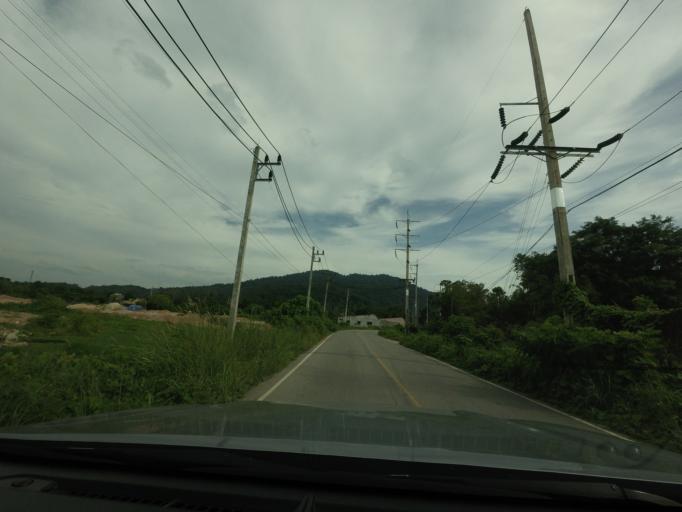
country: TH
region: Yala
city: Yala
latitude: 6.5050
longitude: 101.2875
